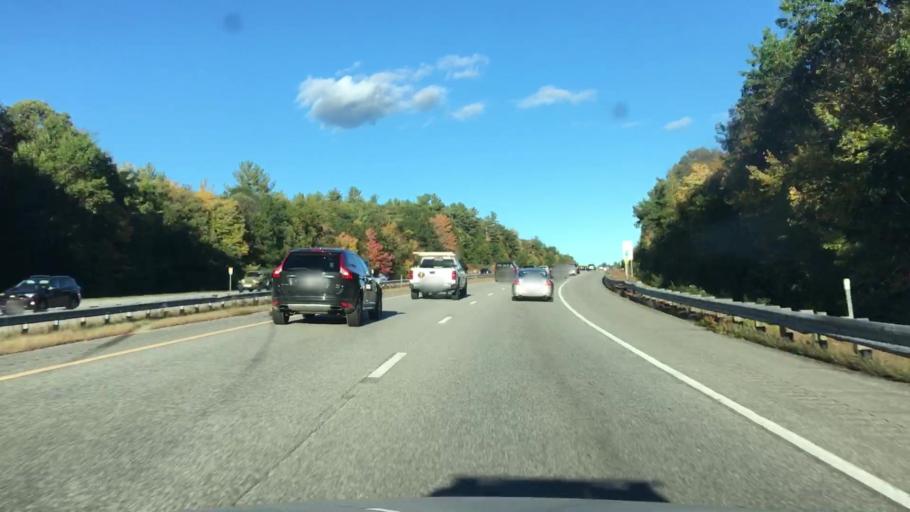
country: US
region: New Hampshire
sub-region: Rockingham County
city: Auburn
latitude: 43.0301
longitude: -71.3556
